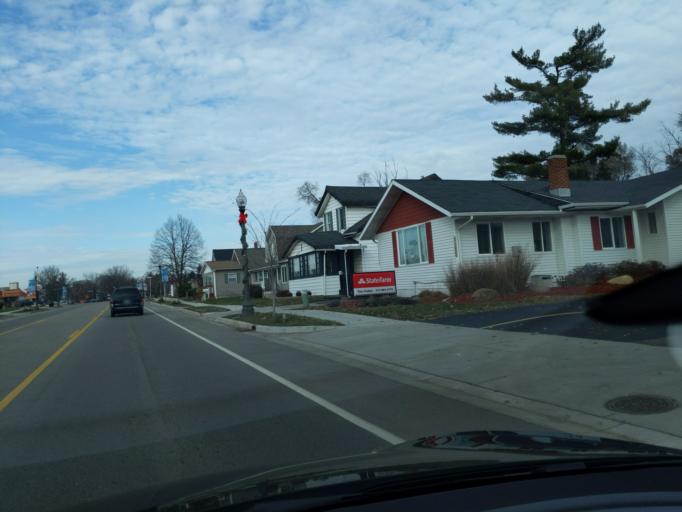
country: US
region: Michigan
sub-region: Ingham County
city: Holt
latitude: 42.6460
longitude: -84.5215
